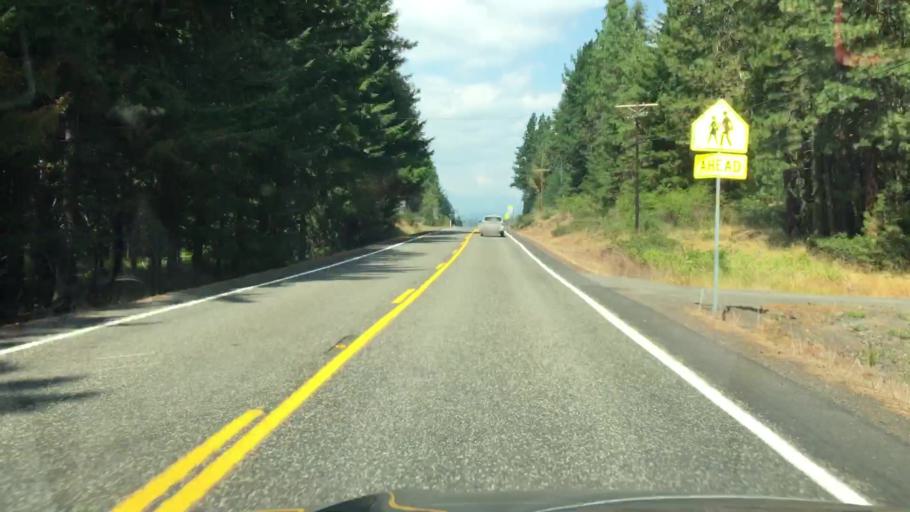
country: US
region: Washington
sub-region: Klickitat County
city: White Salmon
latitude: 45.9855
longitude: -121.5132
